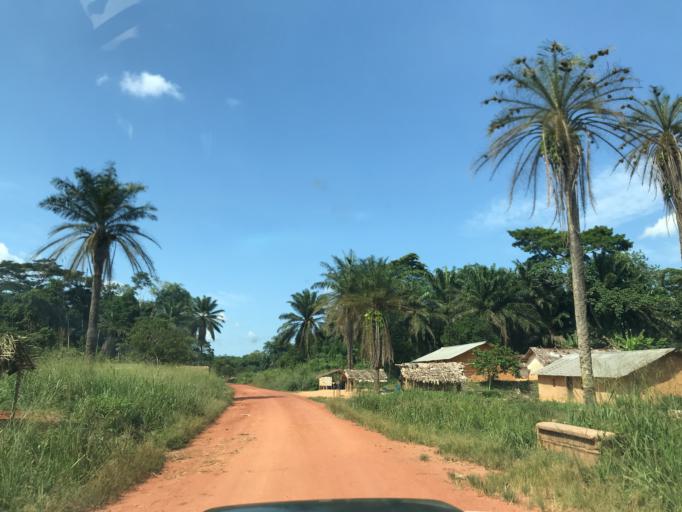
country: CD
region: Eastern Province
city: Kisangani
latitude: 1.1851
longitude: 25.2512
